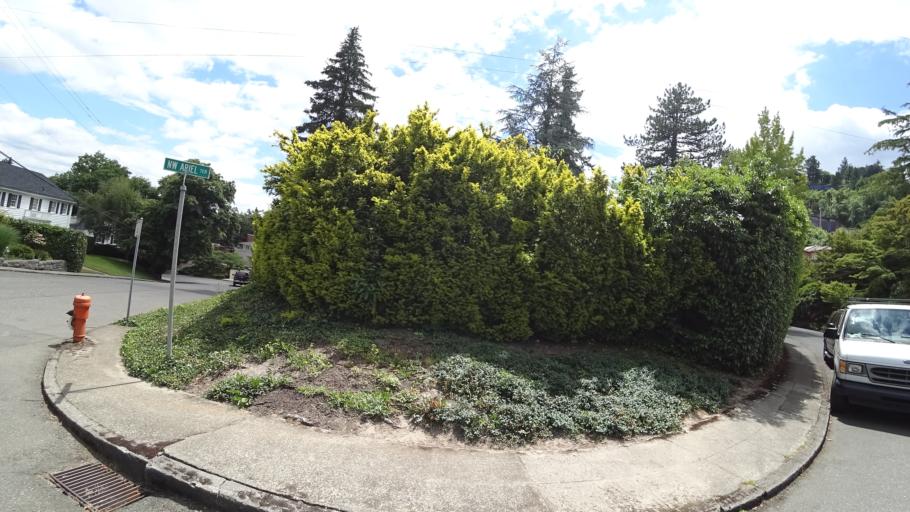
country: US
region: Oregon
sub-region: Multnomah County
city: Portland
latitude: 45.5291
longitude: -122.7109
